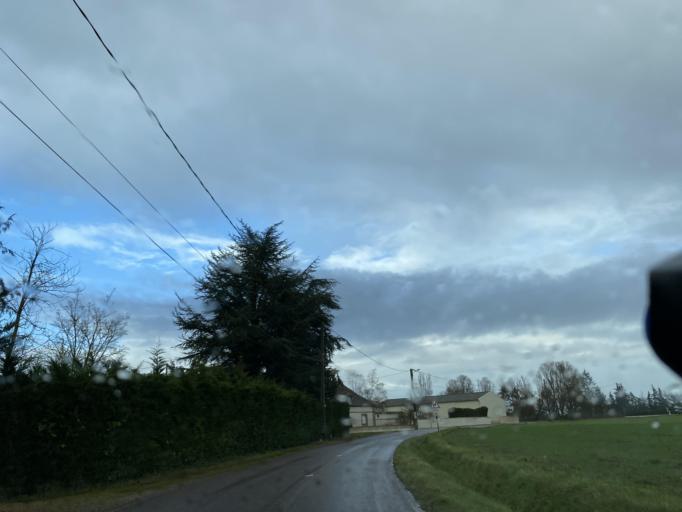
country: FR
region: Haute-Normandie
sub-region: Departement de l'Eure
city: Tillieres-sur-Avre
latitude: 48.7864
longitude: 1.0608
